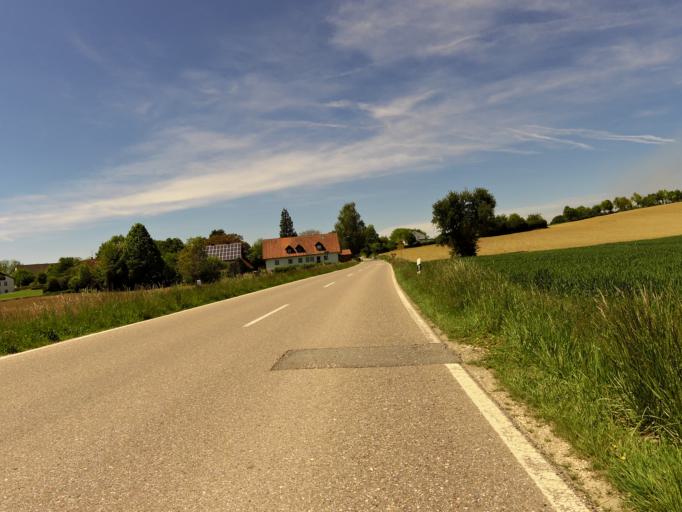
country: DE
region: Bavaria
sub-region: Upper Bavaria
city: Langenbach
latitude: 48.4660
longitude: 11.8672
